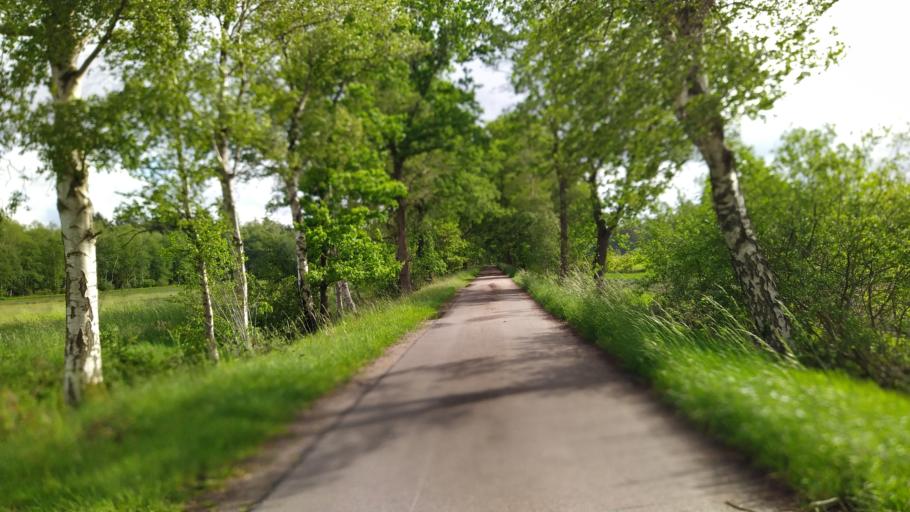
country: DE
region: Lower Saxony
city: Farven
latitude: 53.4236
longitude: 9.3511
